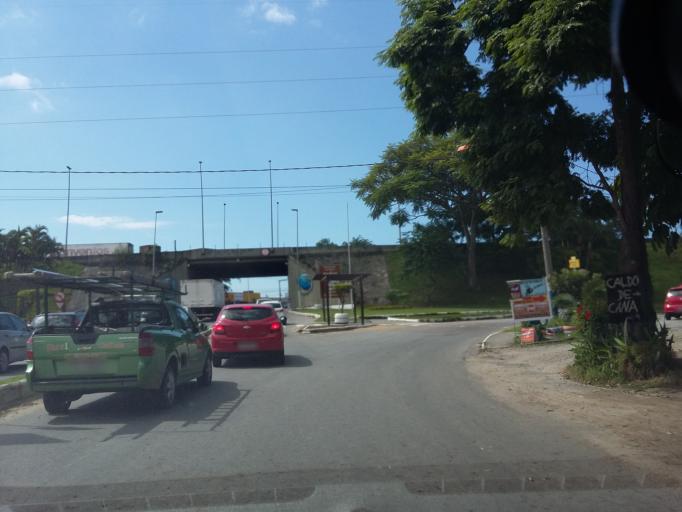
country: BR
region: Santa Catarina
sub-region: Balneario Camboriu
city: Balneario Camboriu
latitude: -27.0001
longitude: -48.6463
